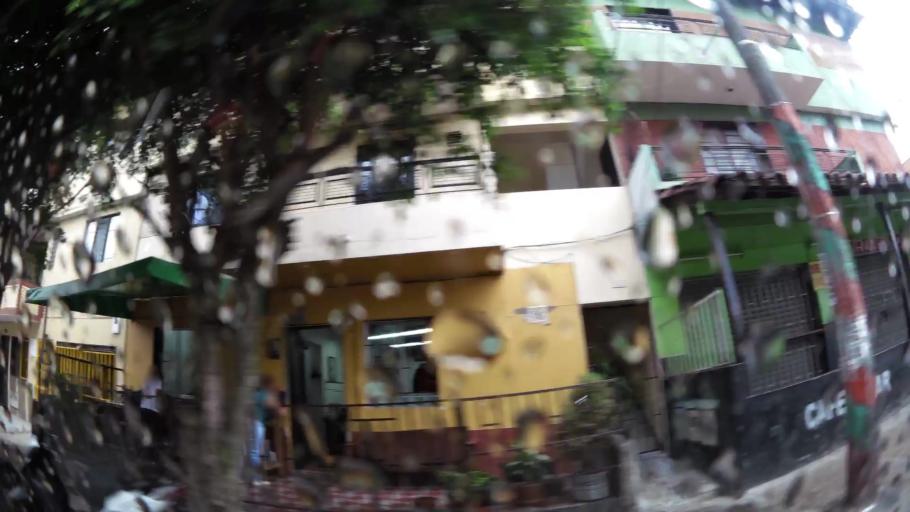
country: CO
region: Antioquia
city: Itagui
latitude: 6.1863
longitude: -75.5951
